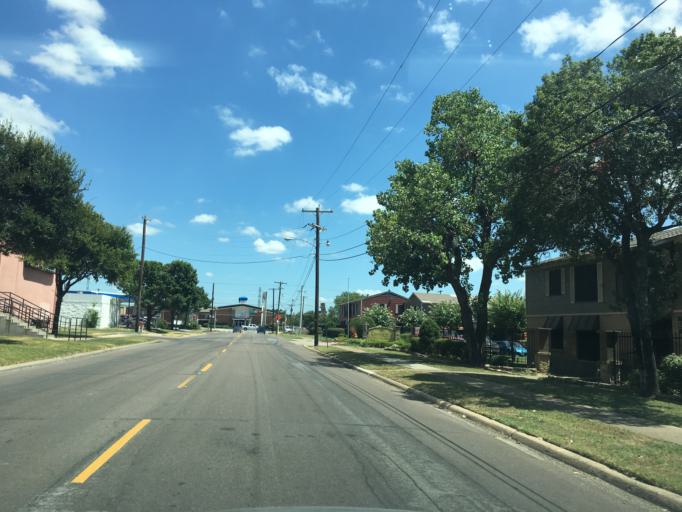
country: US
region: Texas
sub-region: Dallas County
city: Garland
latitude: 32.8482
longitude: -96.6872
